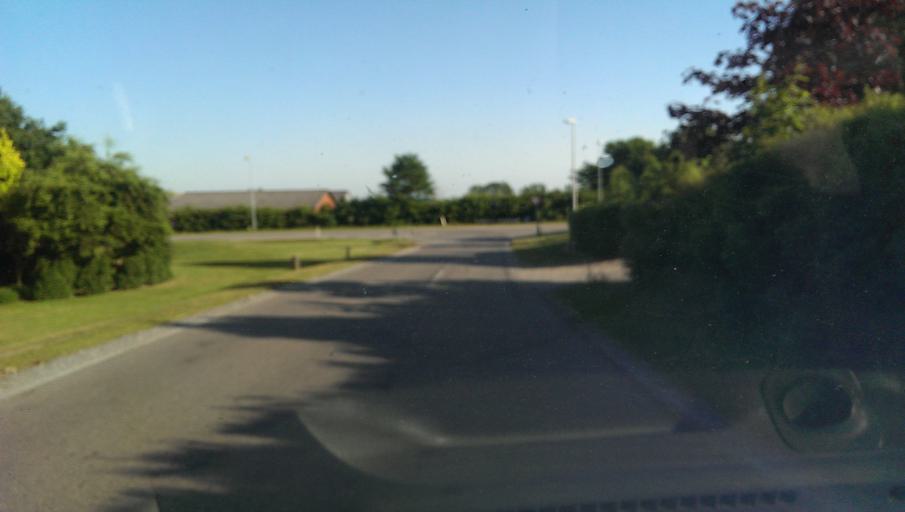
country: DK
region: South Denmark
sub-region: Esbjerg Kommune
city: Bramming
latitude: 55.5273
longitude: 8.6591
